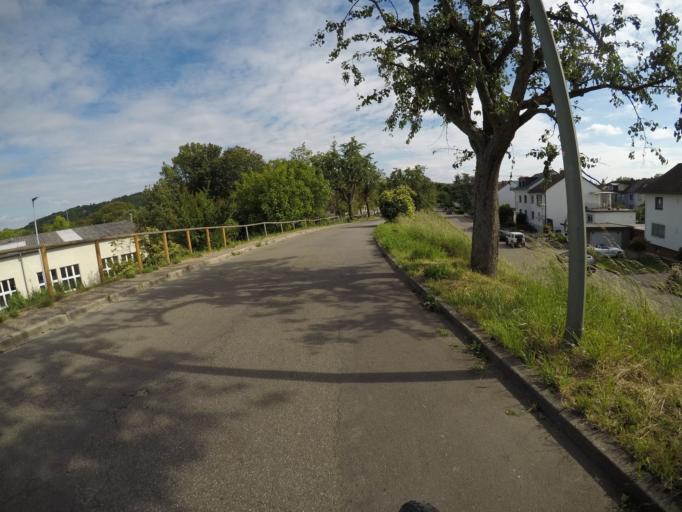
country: DE
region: Baden-Wuerttemberg
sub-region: Karlsruhe Region
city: Karlsruhe
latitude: 49.0055
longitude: 8.4725
